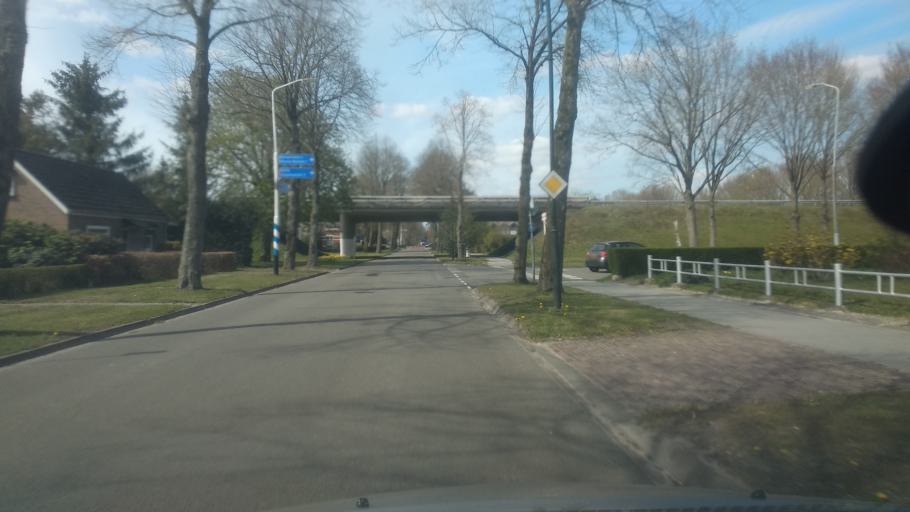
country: NL
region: Drenthe
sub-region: Gemeente Borger-Odoorn
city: Borger
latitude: 52.9294
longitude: 6.8425
